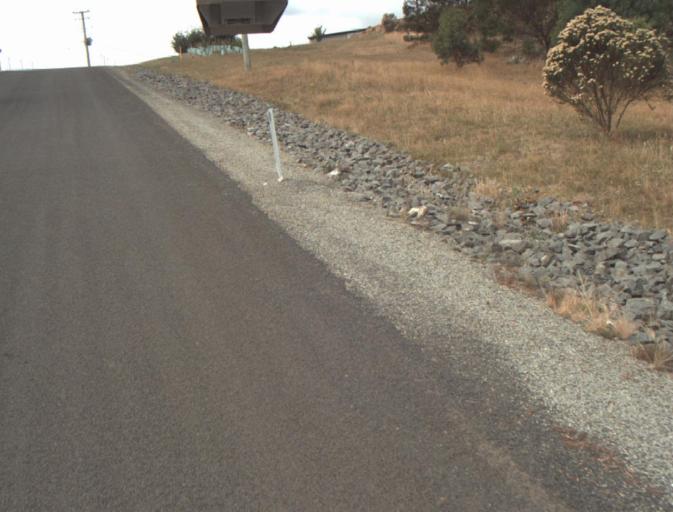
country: AU
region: Tasmania
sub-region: Launceston
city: Mayfield
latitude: -41.3005
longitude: 147.0442
